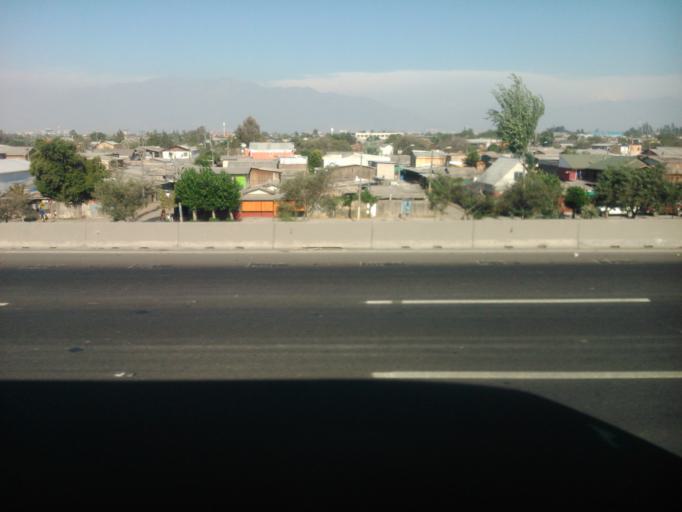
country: CL
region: Santiago Metropolitan
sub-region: Provincia de Maipo
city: San Bernardo
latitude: -33.5300
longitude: -70.7060
